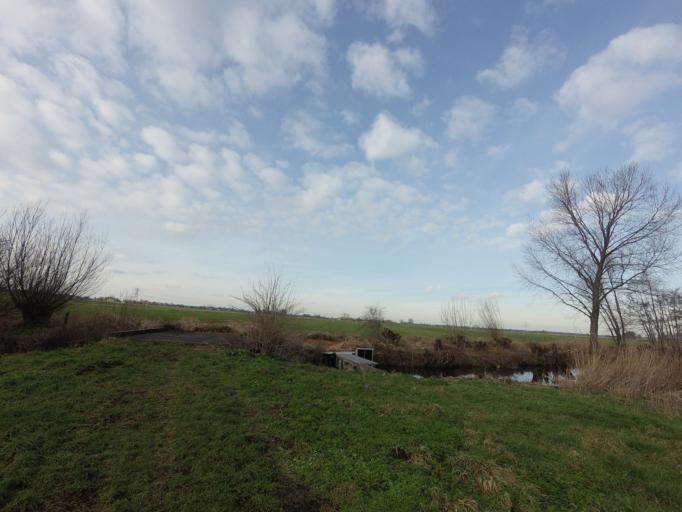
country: NL
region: Utrecht
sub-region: Gemeente Oudewater
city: Oudewater
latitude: 52.0392
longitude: 4.8674
